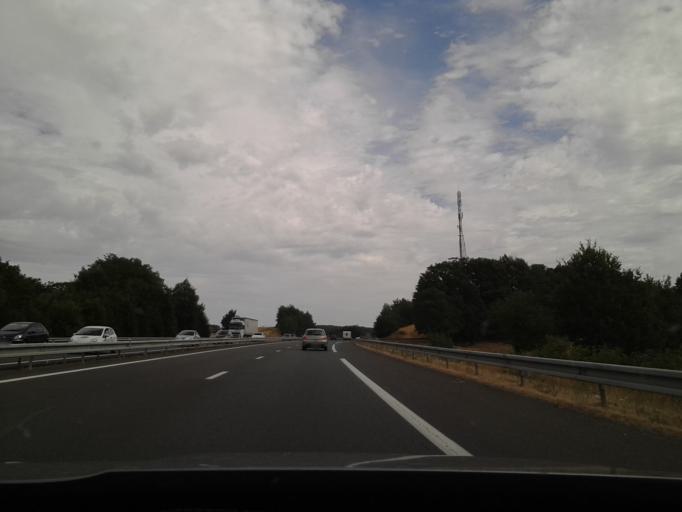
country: FR
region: Pays de la Loire
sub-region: Departement de la Sarthe
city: La Chapelle-Saint-Aubin
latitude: 48.0329
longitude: 0.1370
